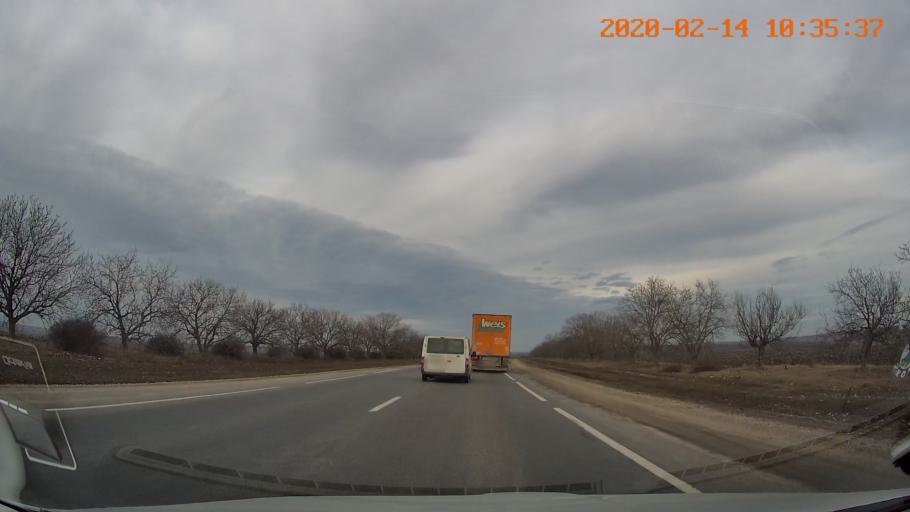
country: MD
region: Riscani
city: Riscani
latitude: 47.9168
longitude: 27.6510
